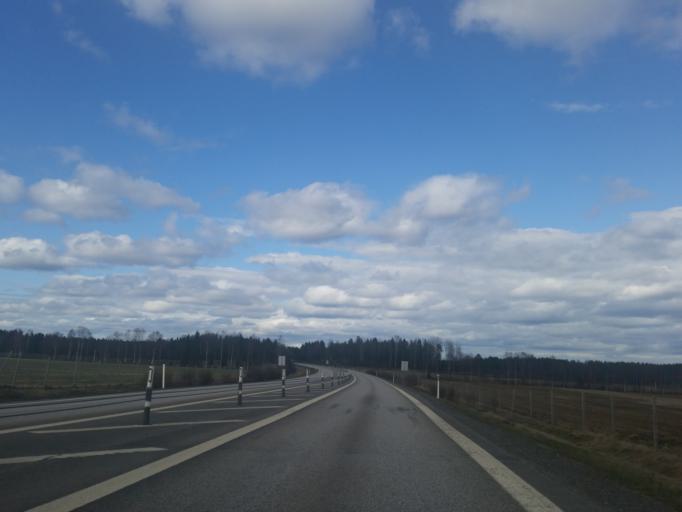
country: SE
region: Vaesterbotten
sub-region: Robertsfors Kommun
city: Robertsfors
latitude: 64.0795
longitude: 20.8655
